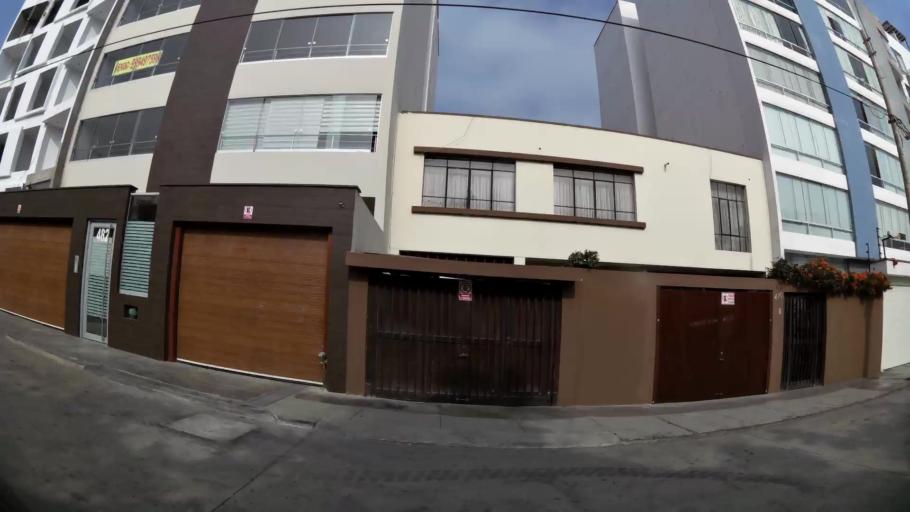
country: PE
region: Lima
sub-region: Lima
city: San Isidro
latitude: -12.0923
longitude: -77.0647
